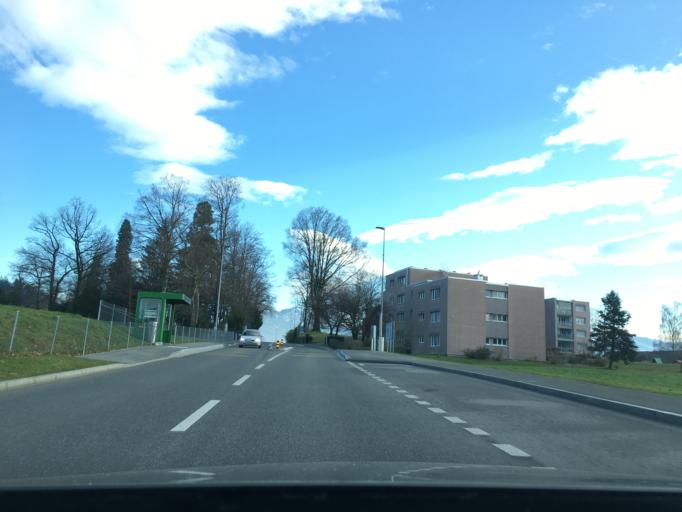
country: CH
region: Lucerne
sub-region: Lucerne-Land District
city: Adligenswil
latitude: 47.0514
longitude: 8.3530
